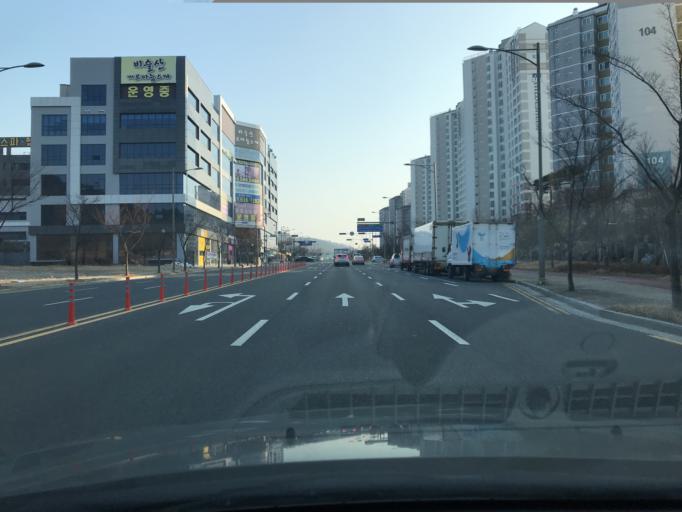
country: KR
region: Daegu
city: Hwawon
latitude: 35.6950
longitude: 128.4698
